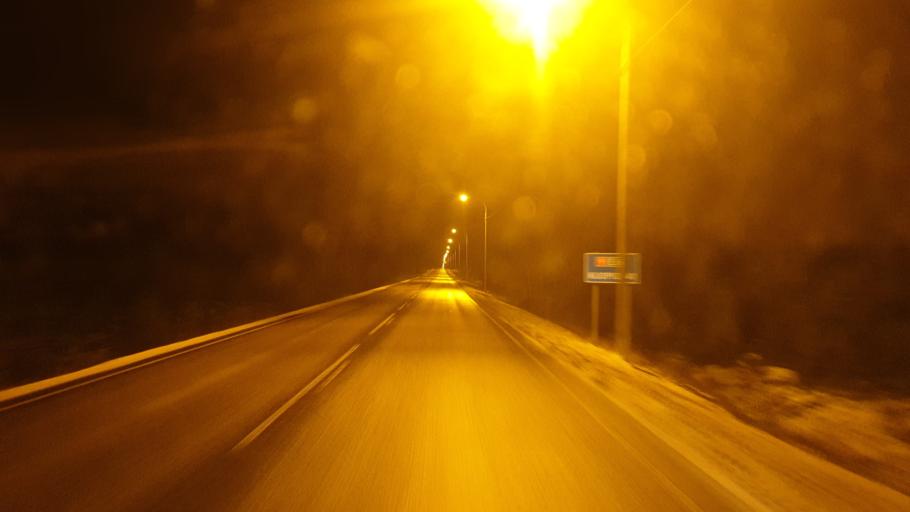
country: FI
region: Northern Savo
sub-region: Sisae-Savo
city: Suonenjoki
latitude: 62.6482
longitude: 27.2703
